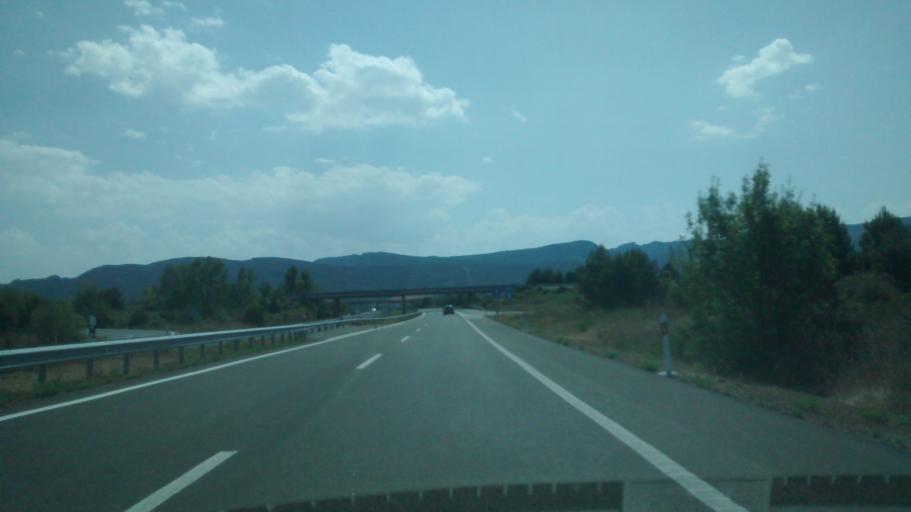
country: ES
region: Basque Country
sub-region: Provincia de Alava
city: Zambrana
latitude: 42.6774
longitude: -2.8895
